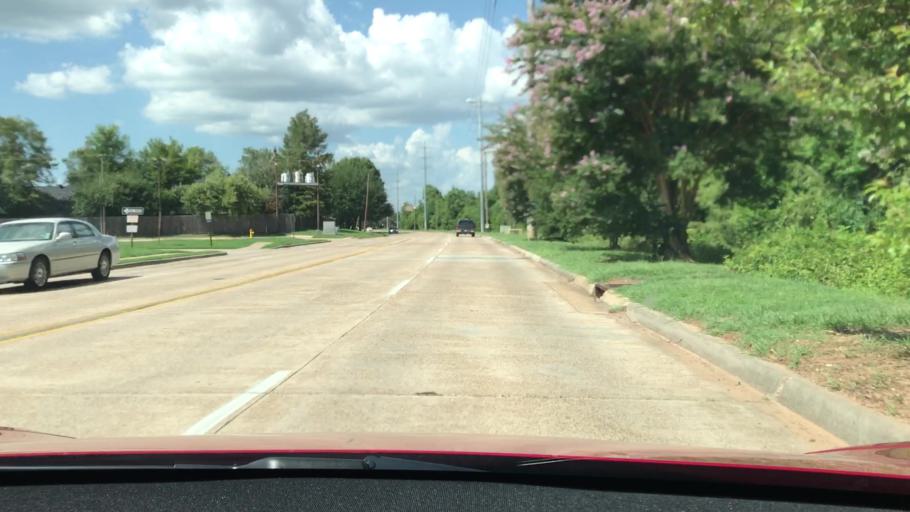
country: US
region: Louisiana
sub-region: Bossier Parish
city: Bossier City
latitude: 32.4483
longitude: -93.7109
